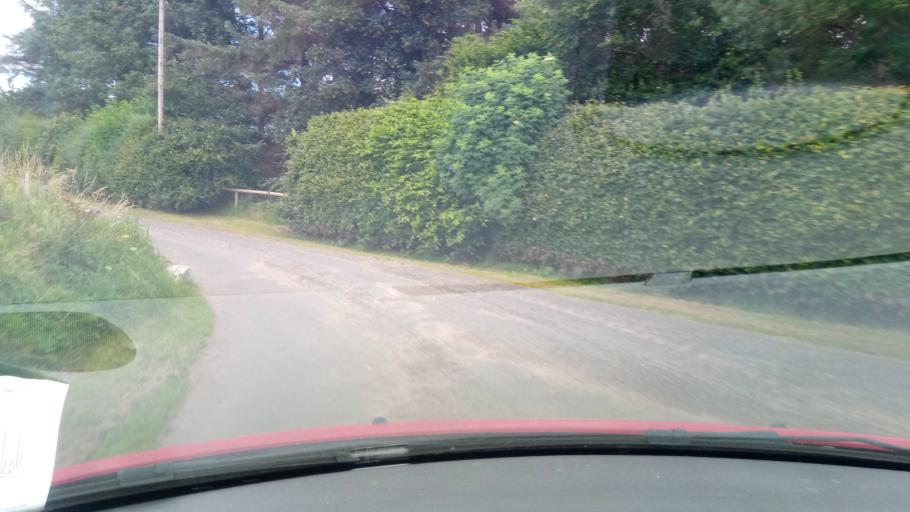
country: GB
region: Scotland
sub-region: The Scottish Borders
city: Jedburgh
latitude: 55.4085
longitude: -2.6174
